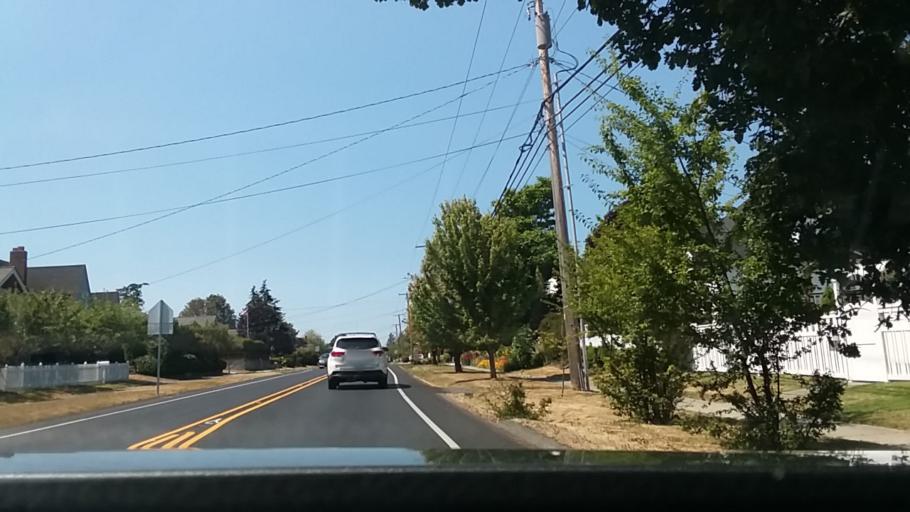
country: US
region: Washington
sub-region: Skagit County
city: Anacortes
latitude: 48.5127
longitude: -122.6208
